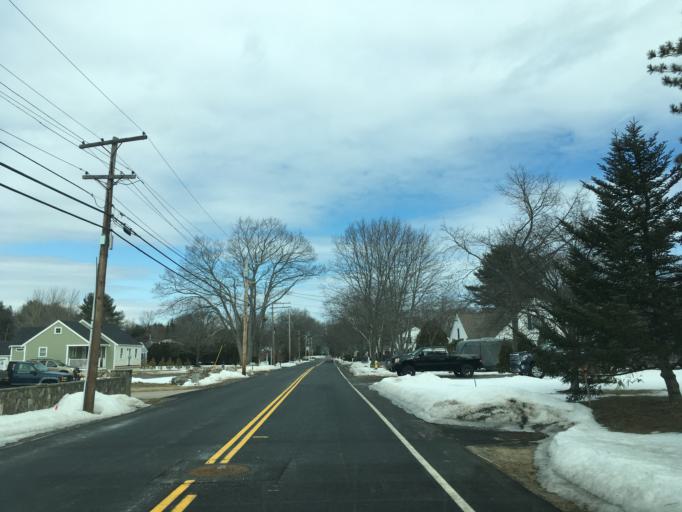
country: US
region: New Hampshire
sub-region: Rockingham County
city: Hampton
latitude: 42.9326
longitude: -70.8222
